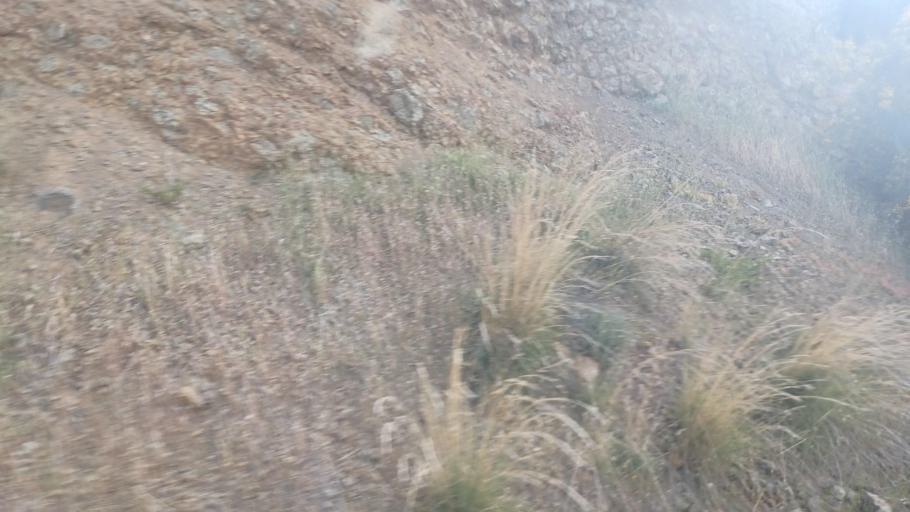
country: CY
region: Pafos
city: Polis
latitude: 34.9911
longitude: 32.3332
